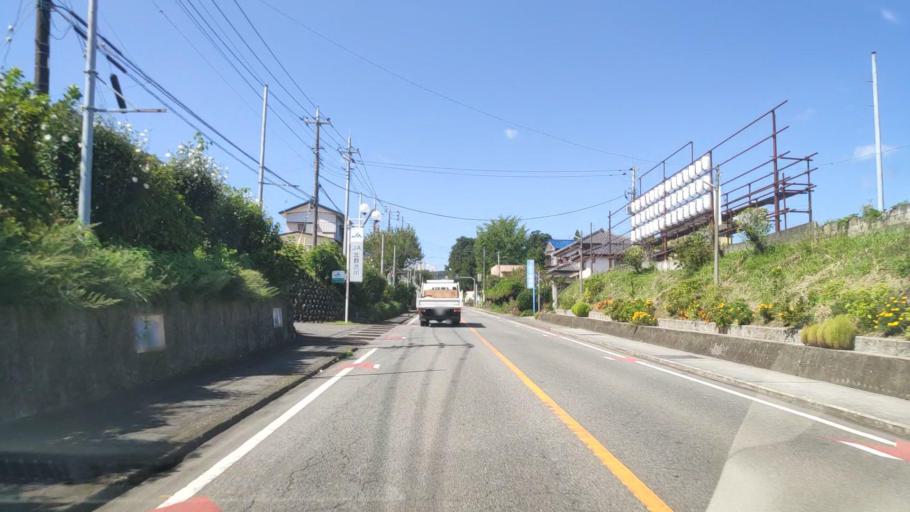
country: JP
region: Gunma
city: Shibukawa
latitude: 36.5009
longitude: 138.9925
